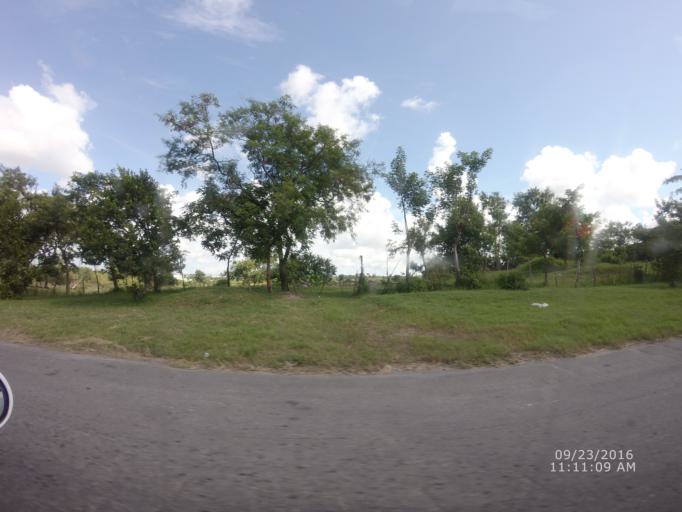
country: CU
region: La Habana
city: Arroyo Naranjo
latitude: 23.0242
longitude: -82.2654
